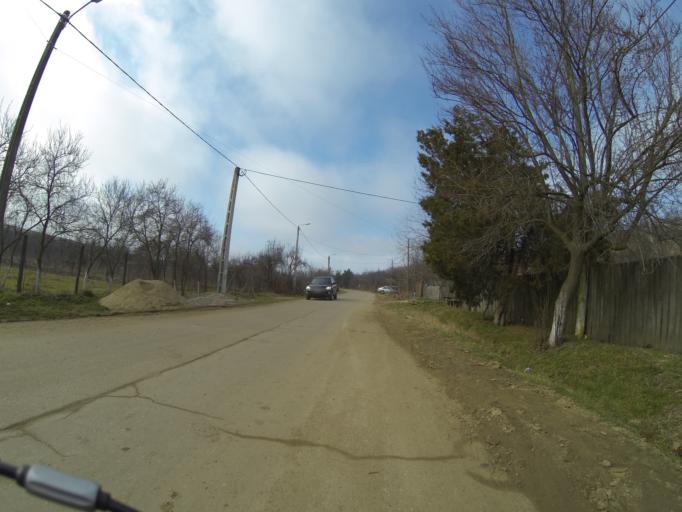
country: RO
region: Mehedinti
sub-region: Comuna Poroina Mare
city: Poroina Mare
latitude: 44.4941
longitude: 22.9960
